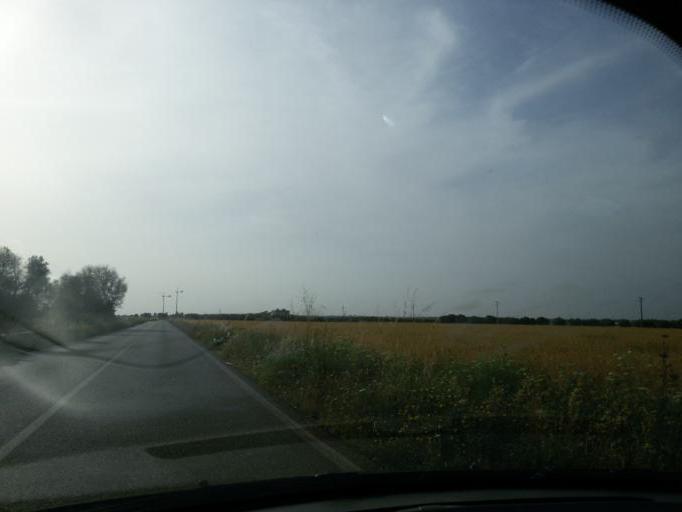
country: IT
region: Apulia
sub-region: Provincia di Lecce
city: Porto Cesareo
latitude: 40.2856
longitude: 17.8806
